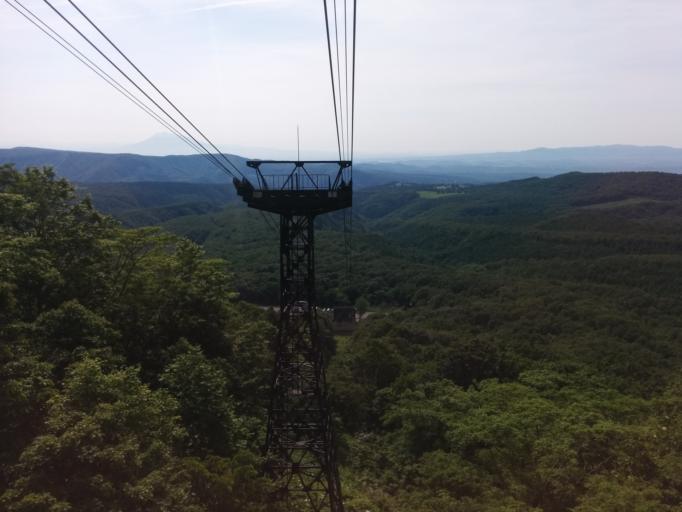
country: JP
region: Aomori
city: Aomori Shi
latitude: 40.6801
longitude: 140.8362
